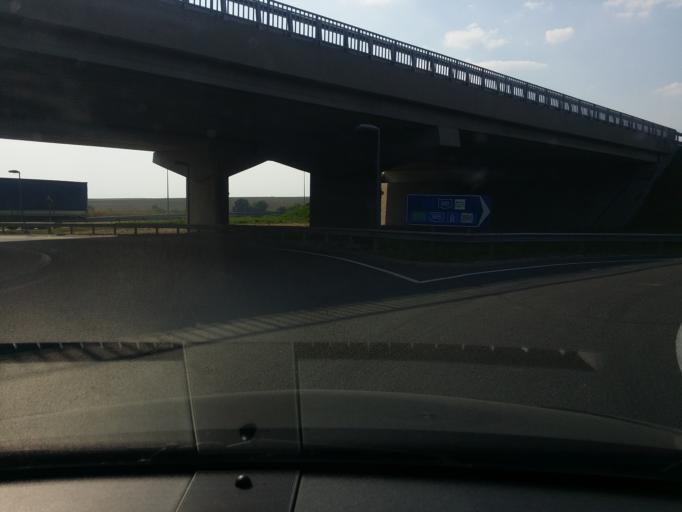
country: HU
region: Fejer
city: Baracs
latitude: 46.9109
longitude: 18.9259
